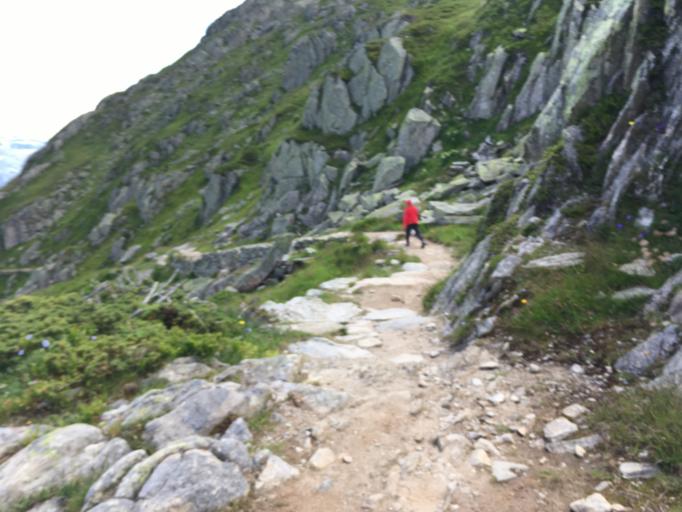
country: CH
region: Valais
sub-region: Goms District
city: Fiesch
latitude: 46.4449
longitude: 8.1192
